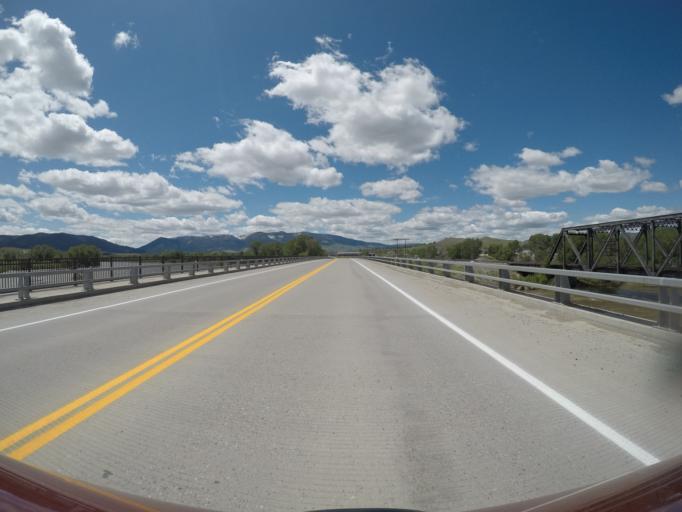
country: US
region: Montana
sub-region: Park County
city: Livingston
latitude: 45.6750
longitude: -110.5365
